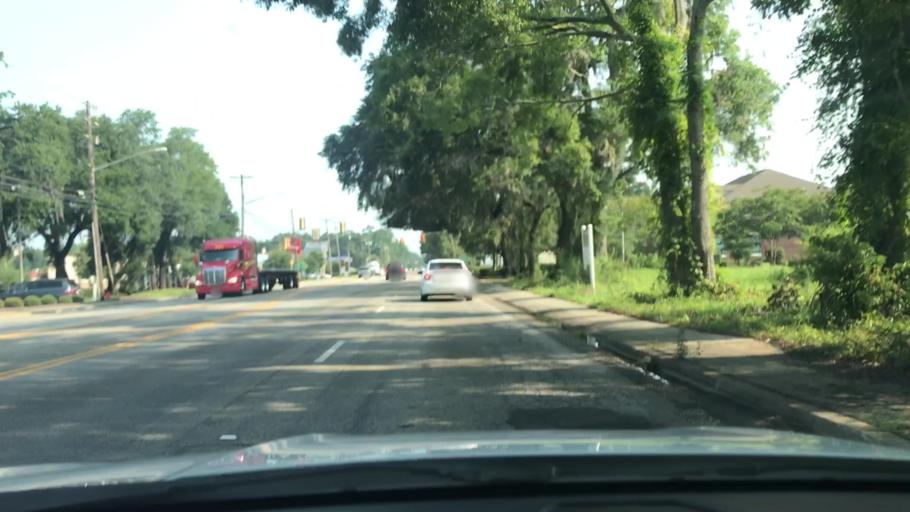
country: US
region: South Carolina
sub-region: Georgetown County
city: Georgetown
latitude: 33.3886
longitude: -79.2890
